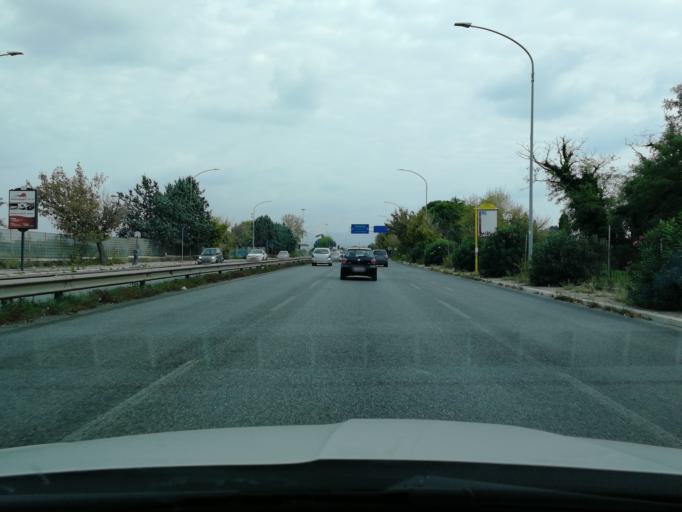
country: IT
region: Latium
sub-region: Citta metropolitana di Roma Capitale
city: Ciampino
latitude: 41.8457
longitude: 12.5797
